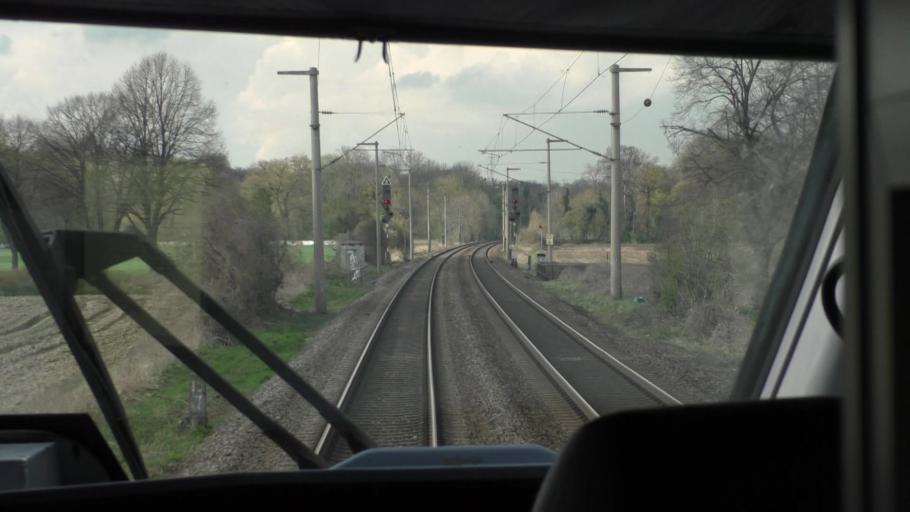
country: DE
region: North Rhine-Westphalia
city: Bruhl
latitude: 50.8204
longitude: 6.9223
